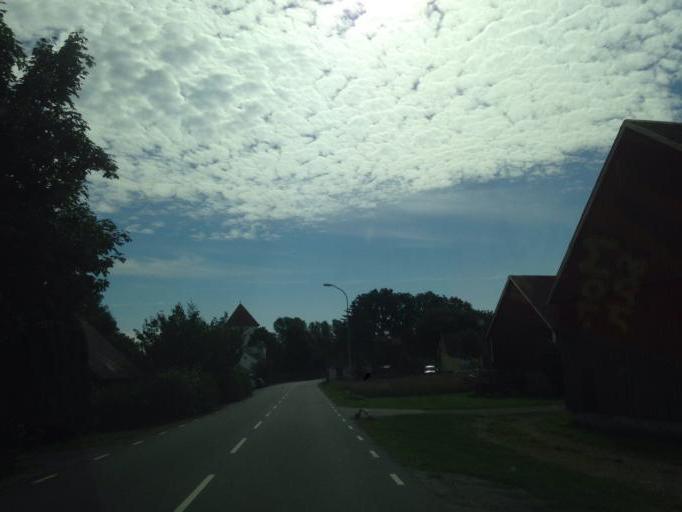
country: SE
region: Skane
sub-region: Tomelilla Kommun
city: Tomelilla
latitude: 55.6218
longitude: 13.8567
